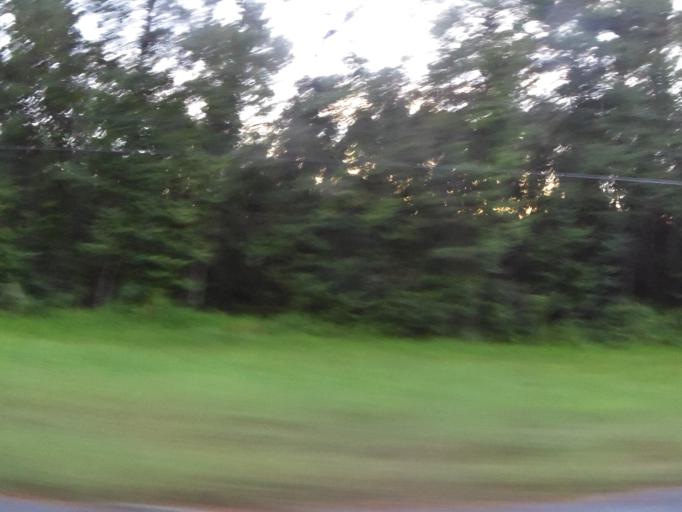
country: US
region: Georgia
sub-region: Camden County
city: Woodbine
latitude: 30.9321
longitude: -81.7164
